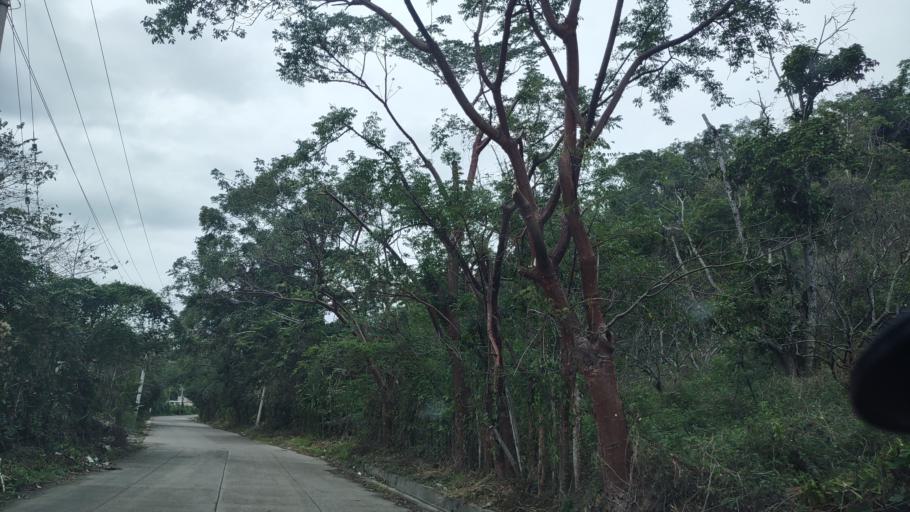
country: MX
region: Veracruz
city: Papantla de Olarte
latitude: 20.4425
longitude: -97.3024
